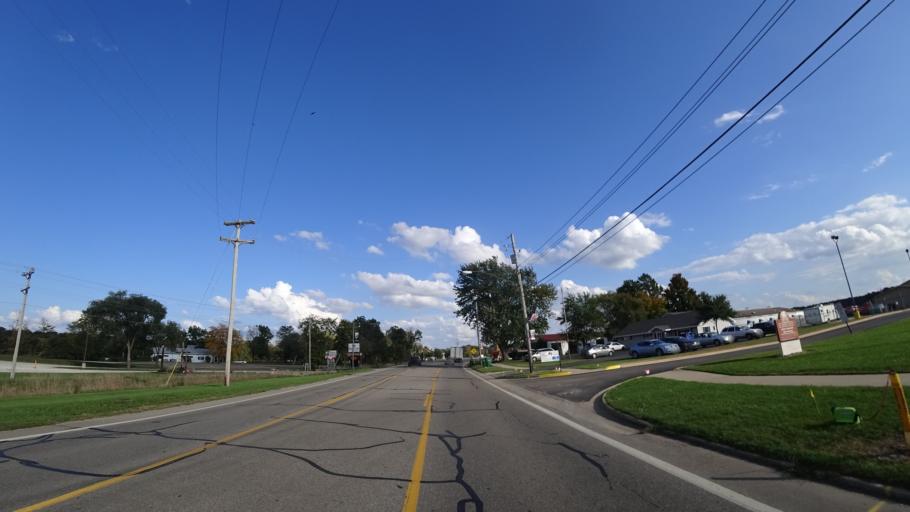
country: US
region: Michigan
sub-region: Saint Joseph County
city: Centreville
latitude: 41.9234
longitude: -85.5146
